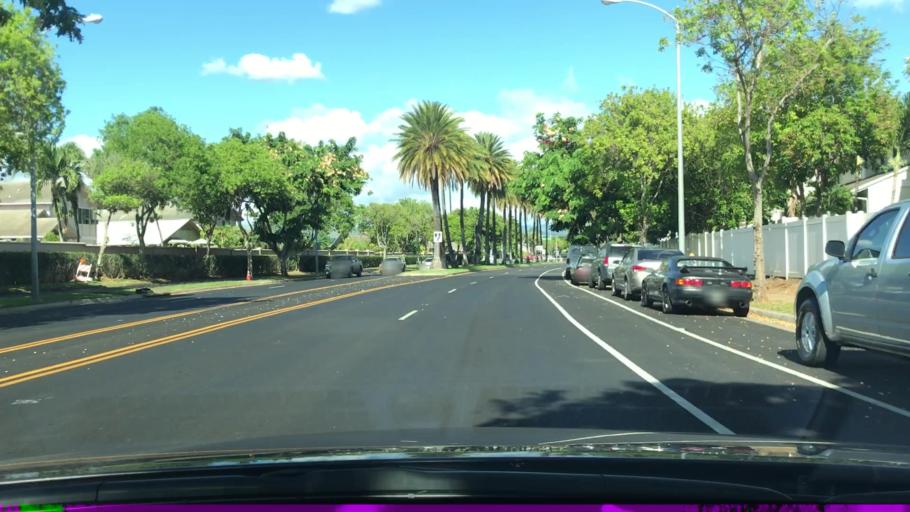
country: US
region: Hawaii
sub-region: Honolulu County
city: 'Ewa Gentry
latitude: 21.3408
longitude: -158.0272
